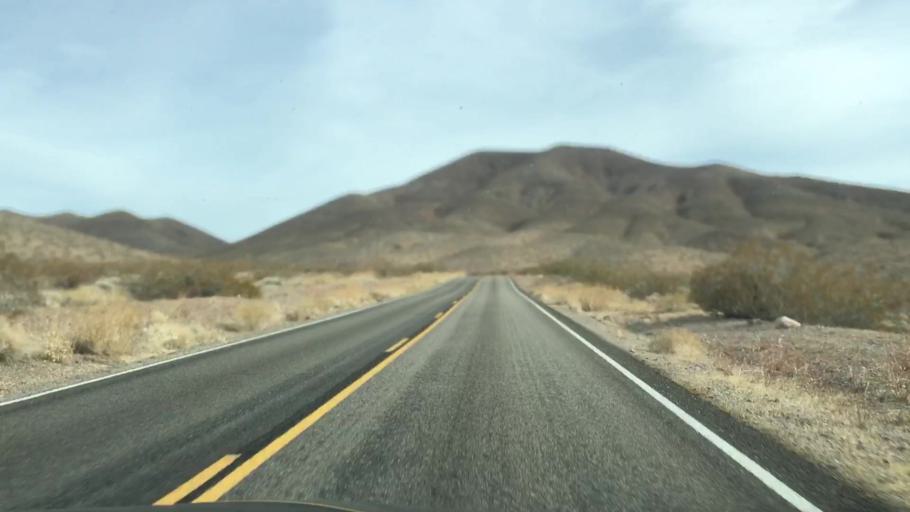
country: US
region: Nevada
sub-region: Nye County
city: Beatty
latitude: 36.7579
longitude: -116.9323
